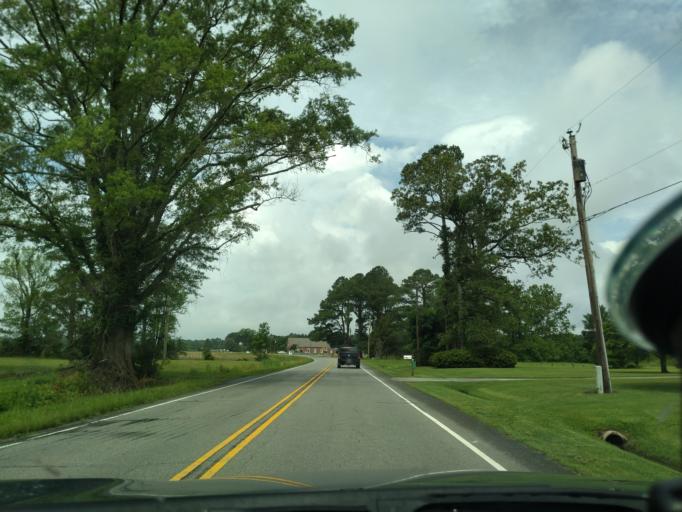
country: US
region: North Carolina
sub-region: Washington County
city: Plymouth
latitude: 35.8759
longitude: -76.6385
